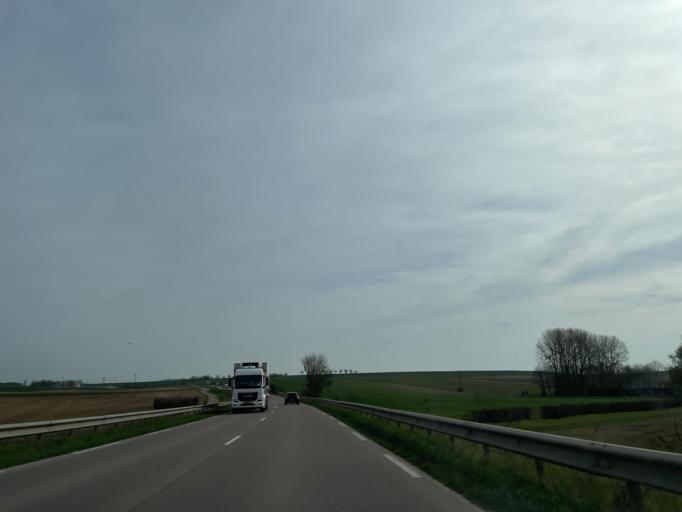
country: FR
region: Champagne-Ardenne
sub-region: Departement de l'Aube
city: Nogent-sur-Seine
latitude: 48.4822
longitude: 3.5002
